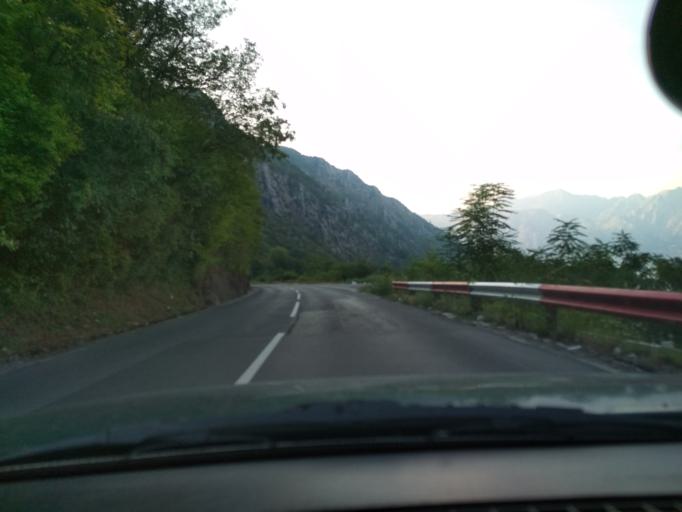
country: ME
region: Kotor
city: Kotor
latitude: 42.4116
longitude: 18.7640
